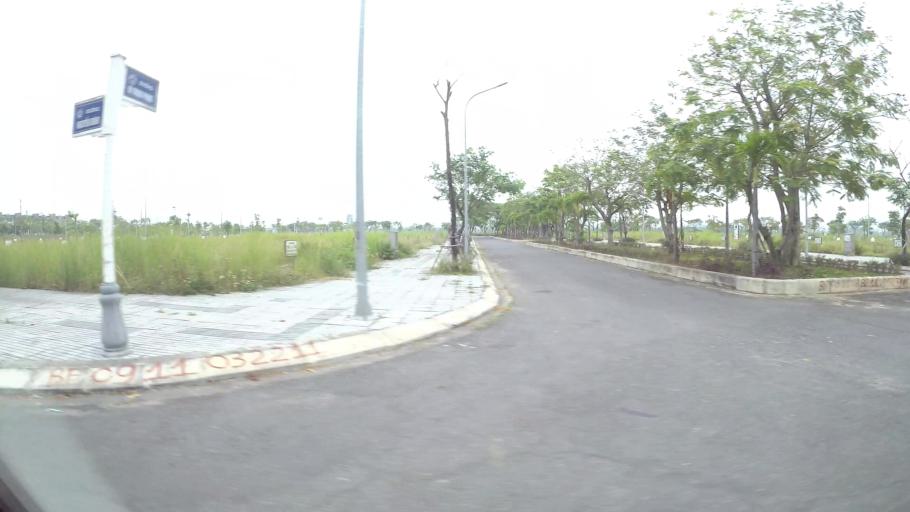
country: VN
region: Da Nang
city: Ngu Hanh Son
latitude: 16.0329
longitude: 108.2318
